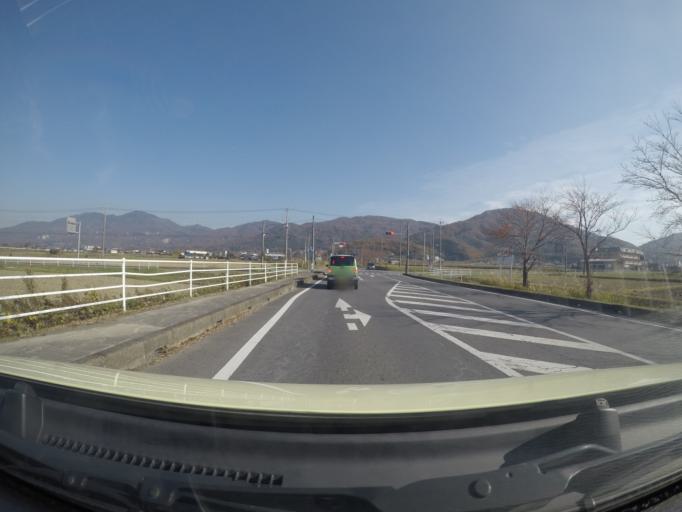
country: JP
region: Ibaraki
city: Makabe
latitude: 36.2685
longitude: 140.0997
